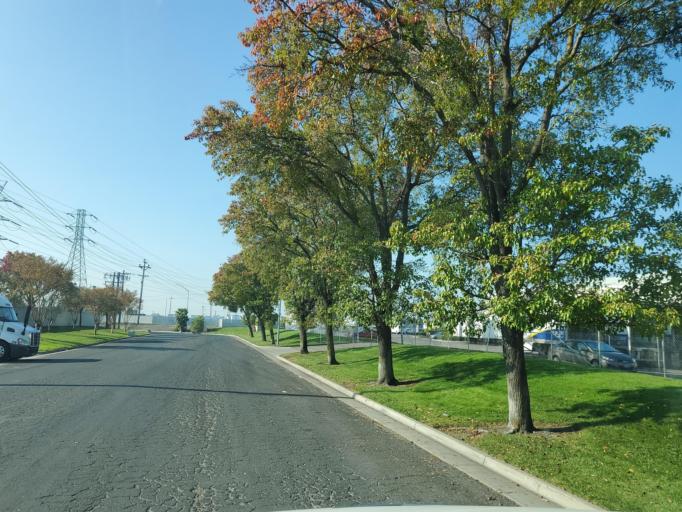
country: US
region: California
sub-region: San Joaquin County
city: Taft Mosswood
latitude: 37.9118
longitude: -121.2691
